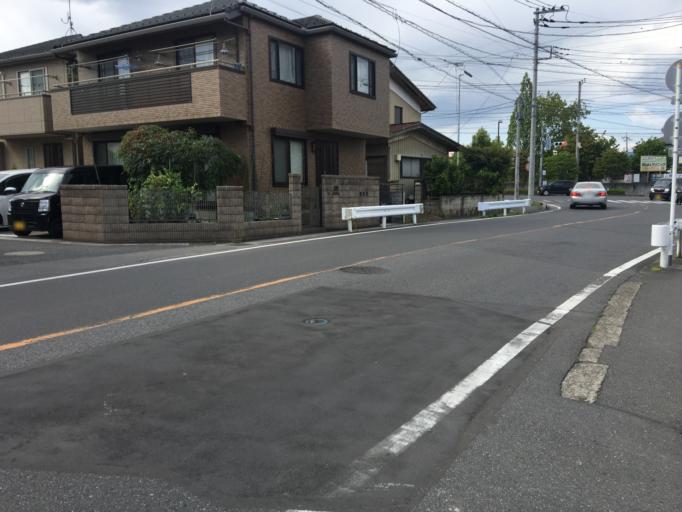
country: JP
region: Saitama
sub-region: Kawaguchi-shi
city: Hatogaya-honcho
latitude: 35.8426
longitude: 139.7400
